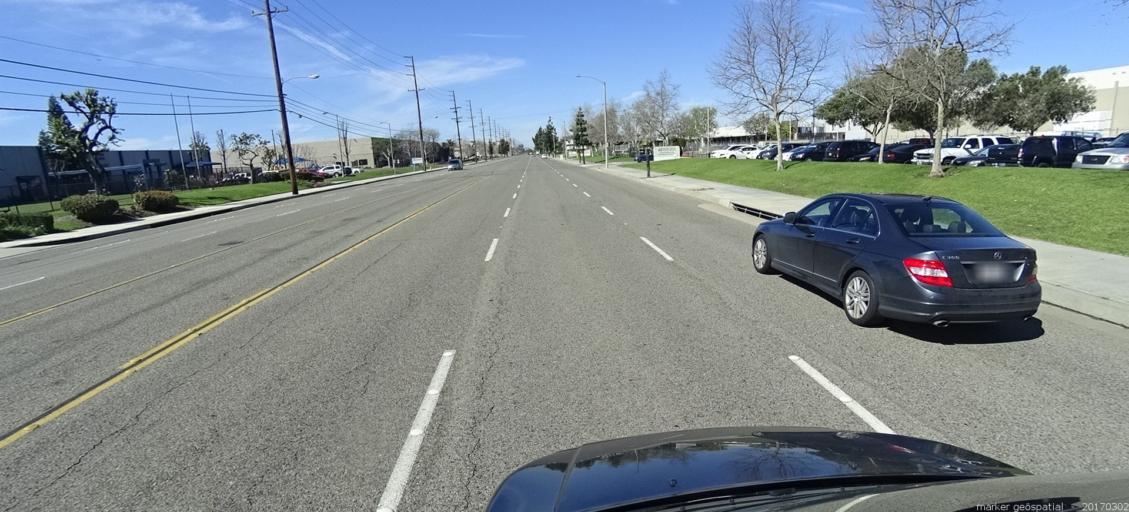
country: US
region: California
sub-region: Orange County
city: Yorba Linda
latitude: 33.8596
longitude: -117.8006
